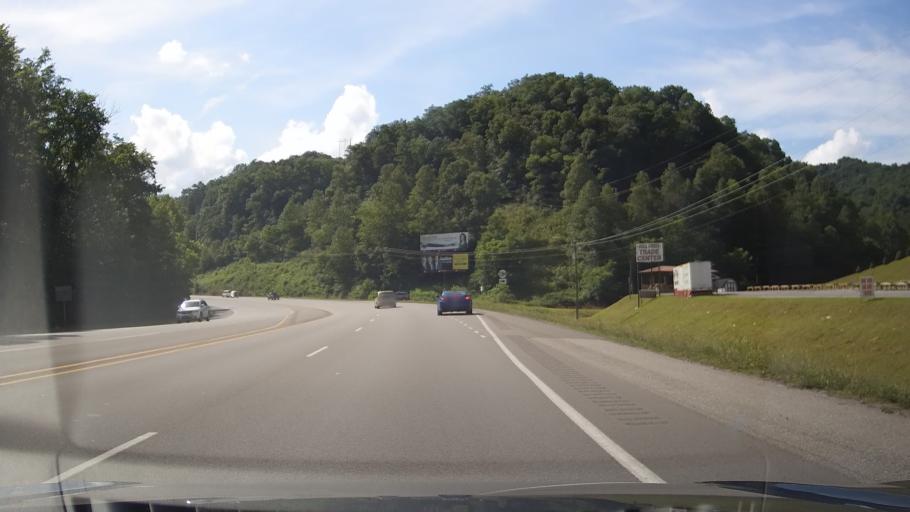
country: US
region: Kentucky
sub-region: Floyd County
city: Prestonsburg
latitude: 37.6410
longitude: -82.7570
